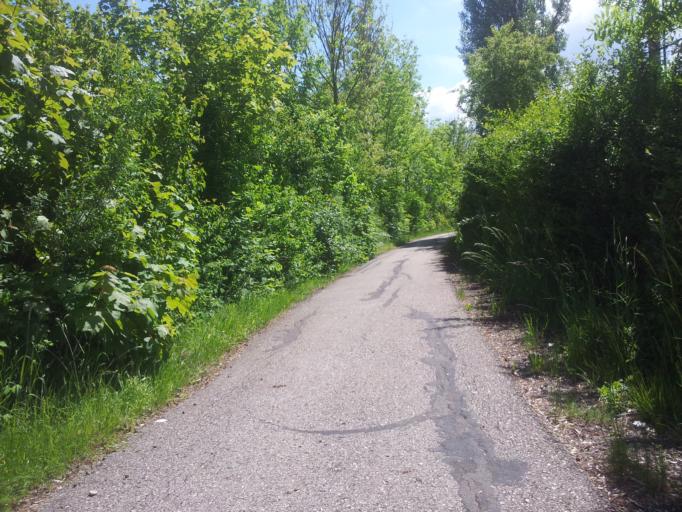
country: DE
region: Baden-Wuerttemberg
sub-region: Regierungsbezirk Stuttgart
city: Unterensingen
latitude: 48.6637
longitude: 9.3625
